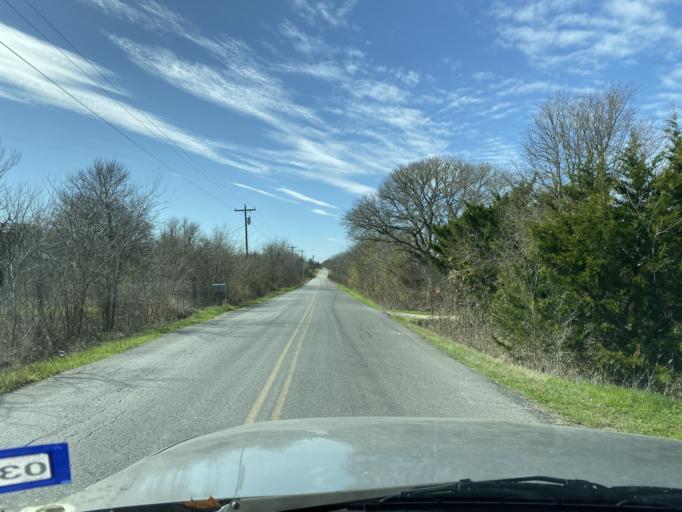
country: US
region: Texas
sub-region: Travis County
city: Onion Creek
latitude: 30.0867
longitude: -97.6998
